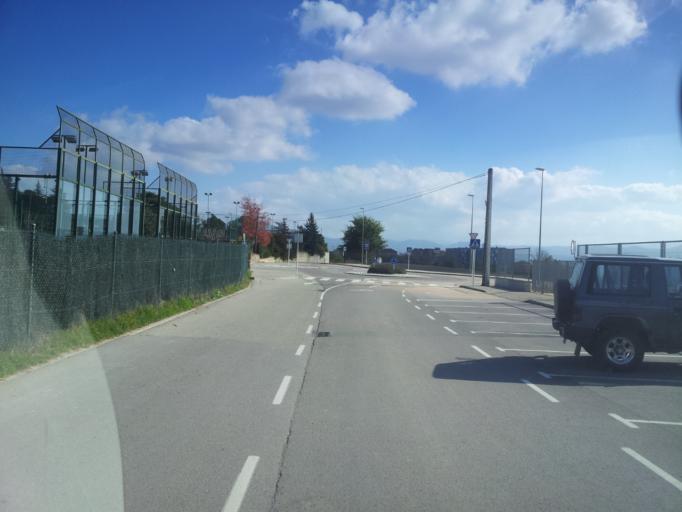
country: ES
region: Catalonia
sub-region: Provincia de Barcelona
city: Gurb
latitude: 41.9334
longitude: 2.2337
